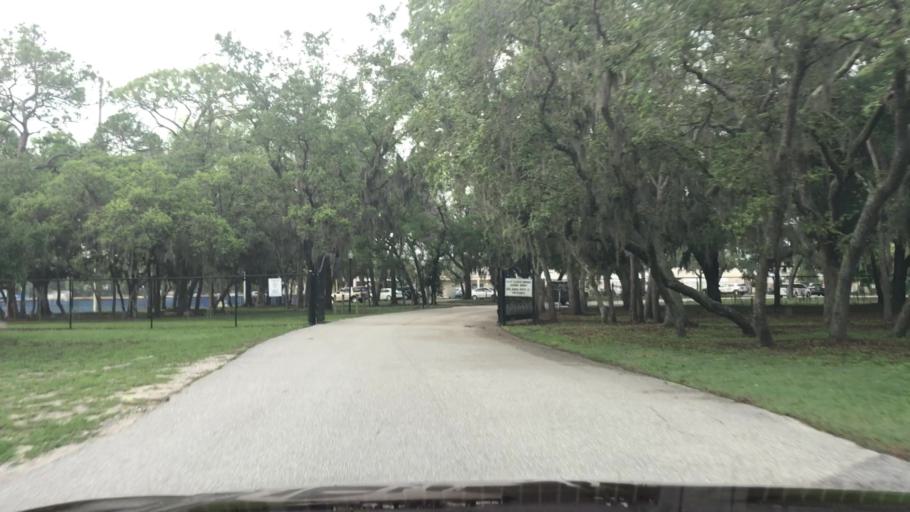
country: US
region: Florida
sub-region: Sarasota County
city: Fruitville
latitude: 27.3263
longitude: -82.4617
